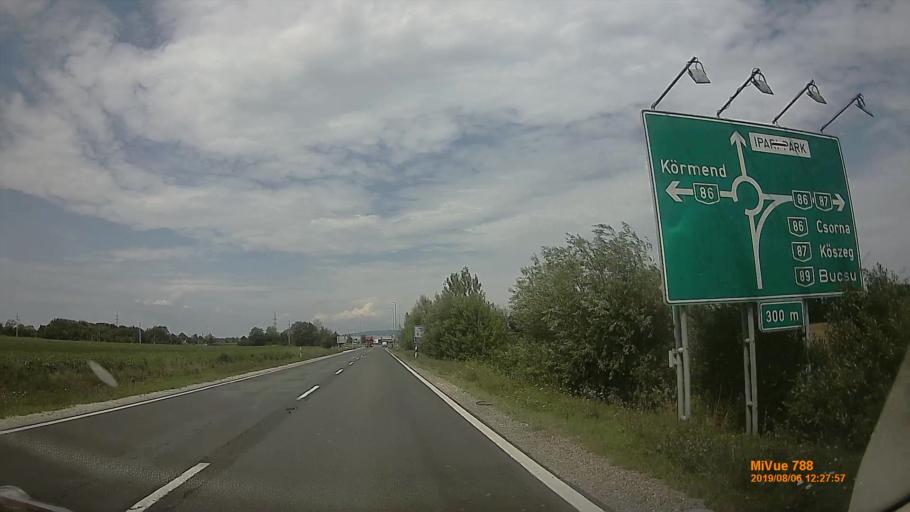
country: HU
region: Vas
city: Szombathely
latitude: 47.2187
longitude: 16.6616
